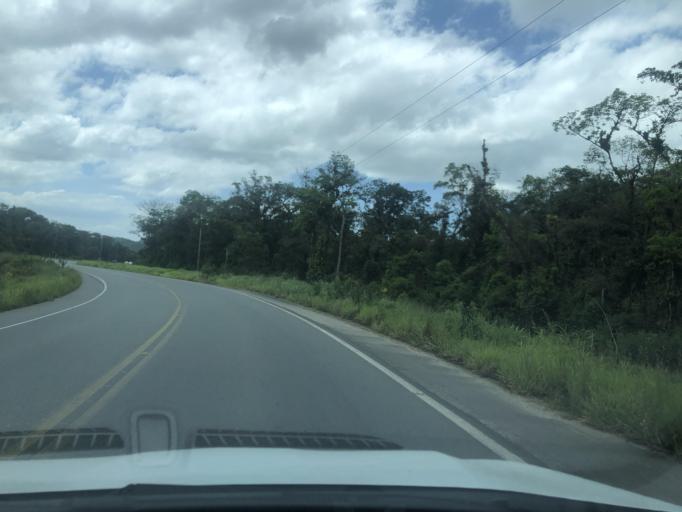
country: BR
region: Santa Catarina
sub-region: Joinville
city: Joinville
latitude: -26.4008
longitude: -48.7572
